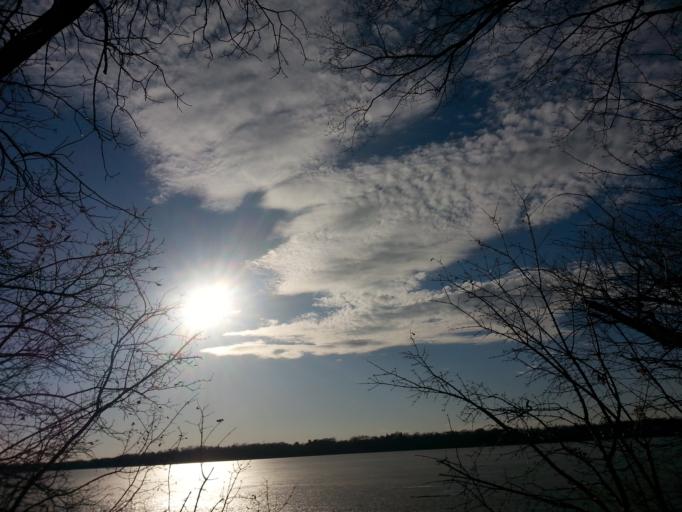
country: US
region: Minnesota
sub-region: Hennepin County
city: Richfield
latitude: 44.9232
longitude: -93.2969
